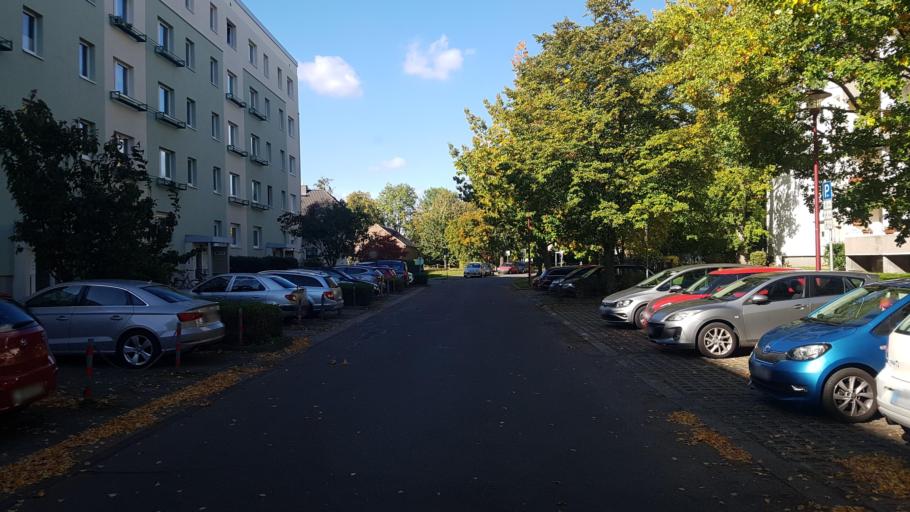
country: DE
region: Brandenburg
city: Cottbus
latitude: 51.7581
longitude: 14.3030
